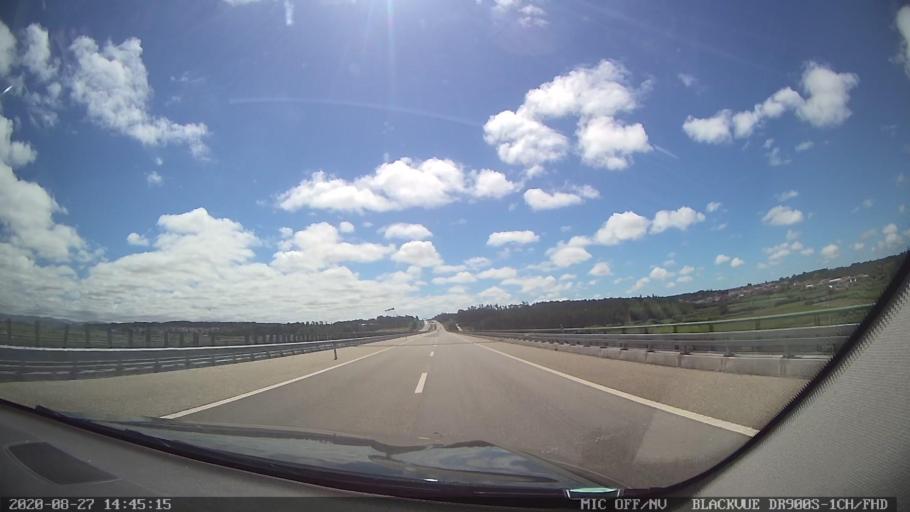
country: PT
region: Leiria
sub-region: Leiria
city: Amor
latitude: 39.8073
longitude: -8.8466
